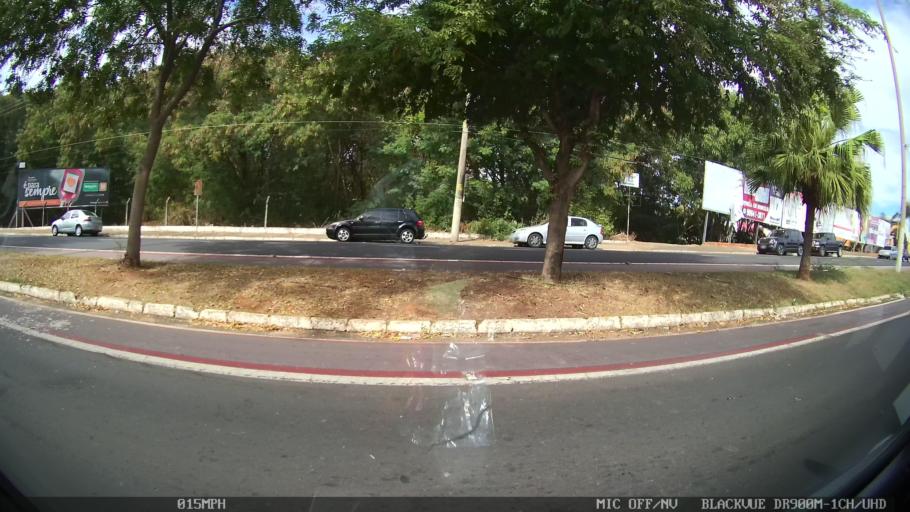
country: BR
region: Sao Paulo
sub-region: Catanduva
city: Catanduva
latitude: -21.1492
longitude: -48.9774
